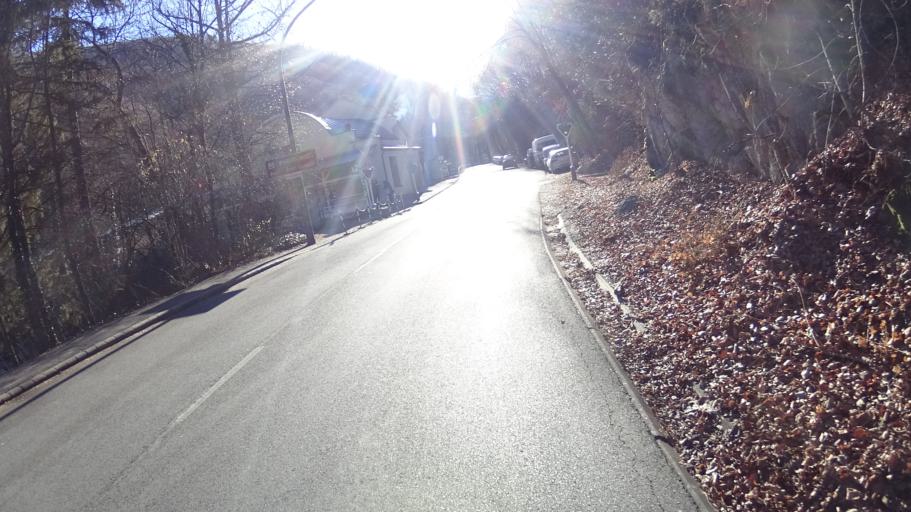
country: HU
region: Borsod-Abauj-Zemplen
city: Sajobabony
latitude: 48.1039
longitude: 20.6222
